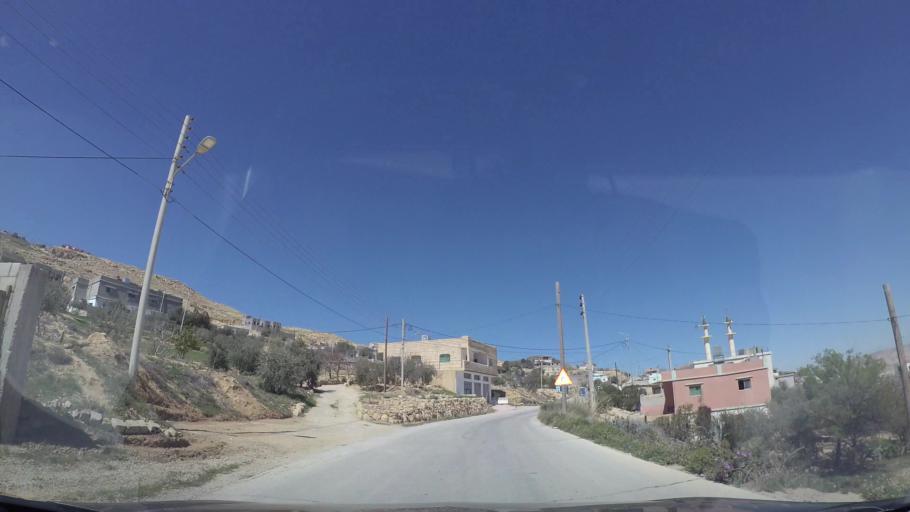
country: JO
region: Tafielah
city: At Tafilah
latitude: 30.8346
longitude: 35.5756
